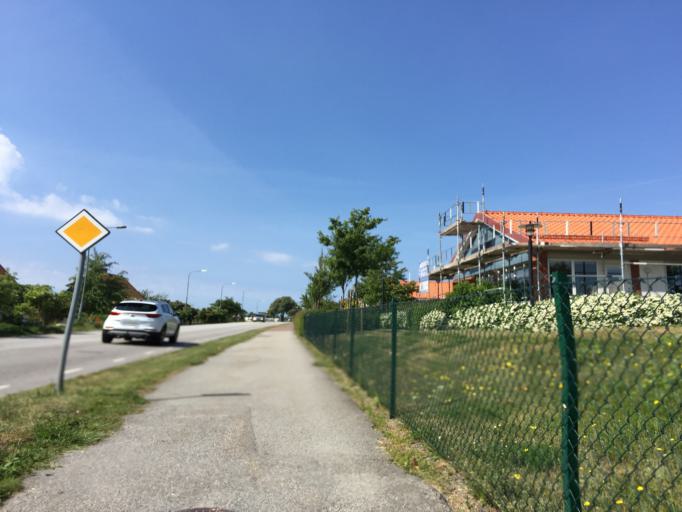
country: SE
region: Skane
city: Smygehamn
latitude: 55.3418
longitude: 13.3680
